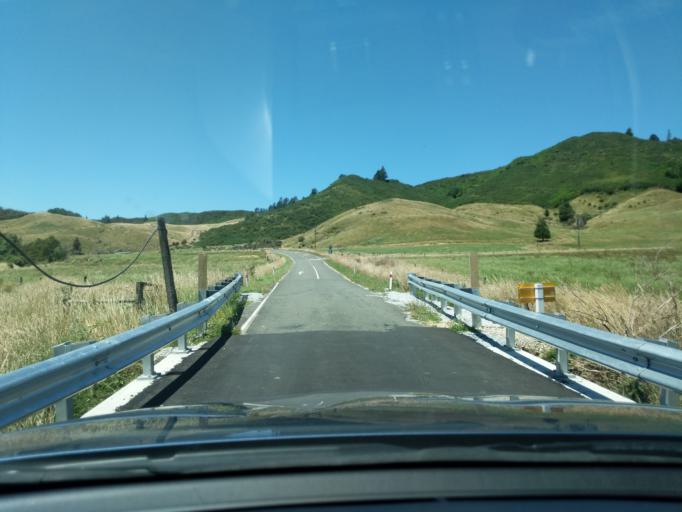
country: NZ
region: Tasman
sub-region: Tasman District
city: Takaka
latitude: -40.7388
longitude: 172.5773
